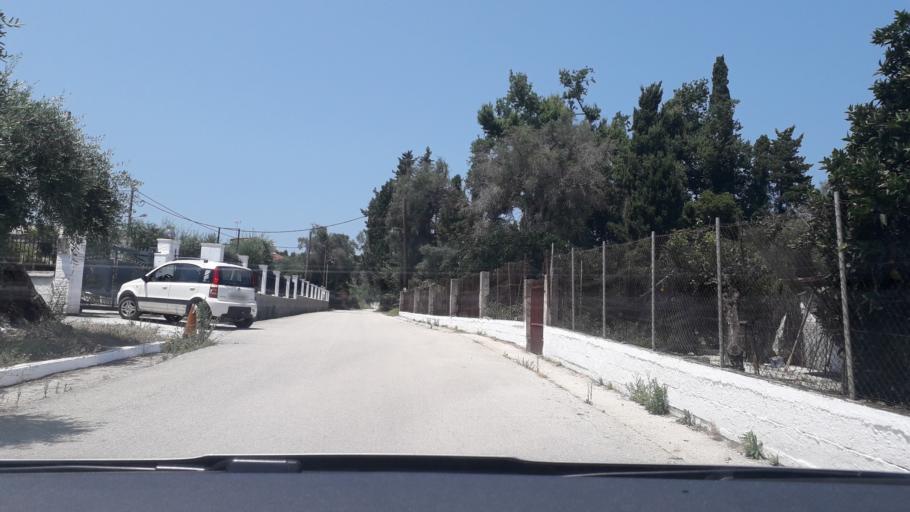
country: GR
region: Ionian Islands
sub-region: Nomos Kerkyras
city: Lefkimmi
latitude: 39.3787
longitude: 20.1128
